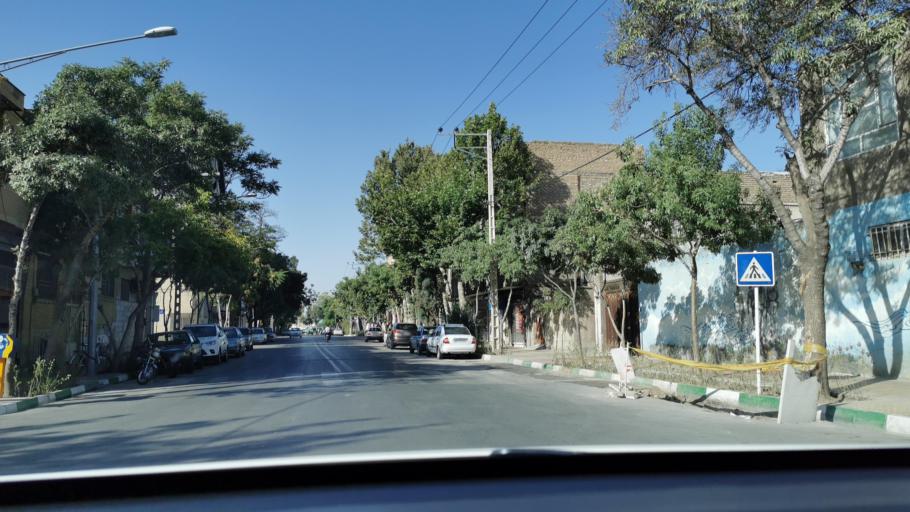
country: IR
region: Razavi Khorasan
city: Mashhad
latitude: 36.3008
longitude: 59.6213
